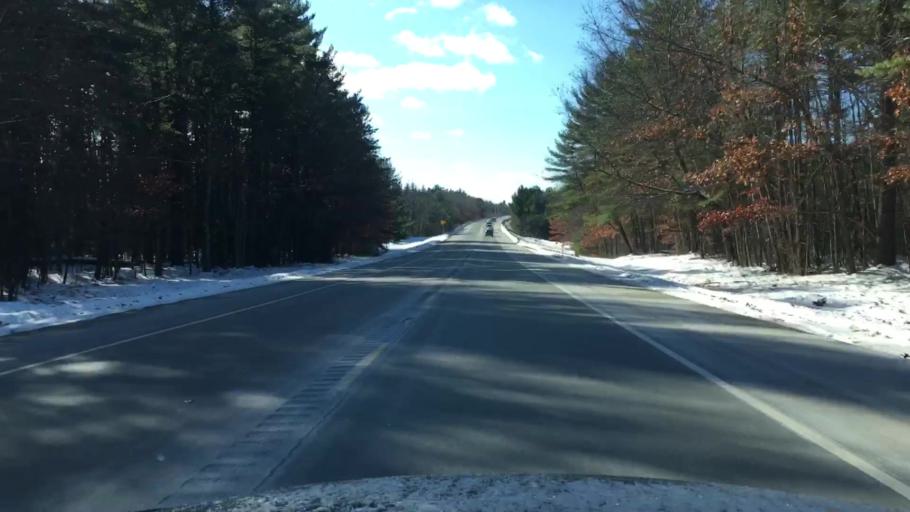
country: US
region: New Hampshire
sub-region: Hillsborough County
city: Milford
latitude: 42.8500
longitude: -71.6124
